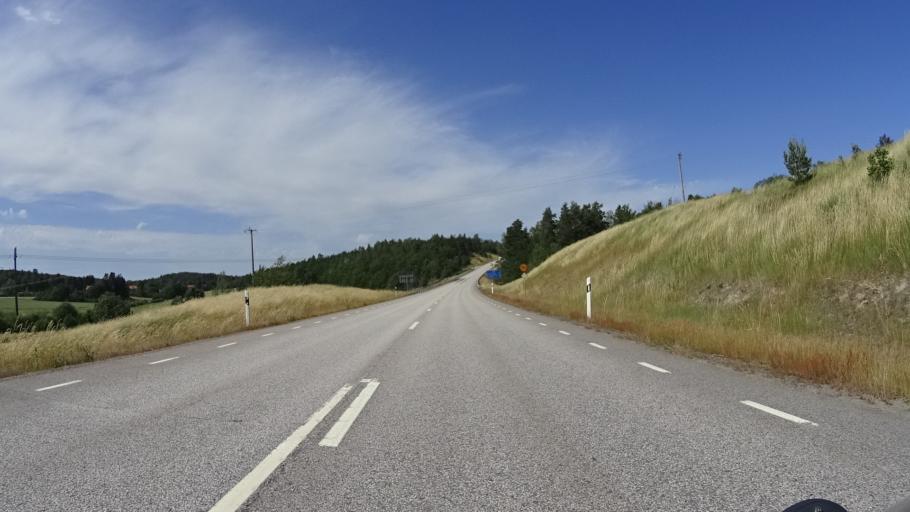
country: SE
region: Kalmar
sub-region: Vasterviks Kommun
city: Gamleby
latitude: 57.9169
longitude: 16.3757
